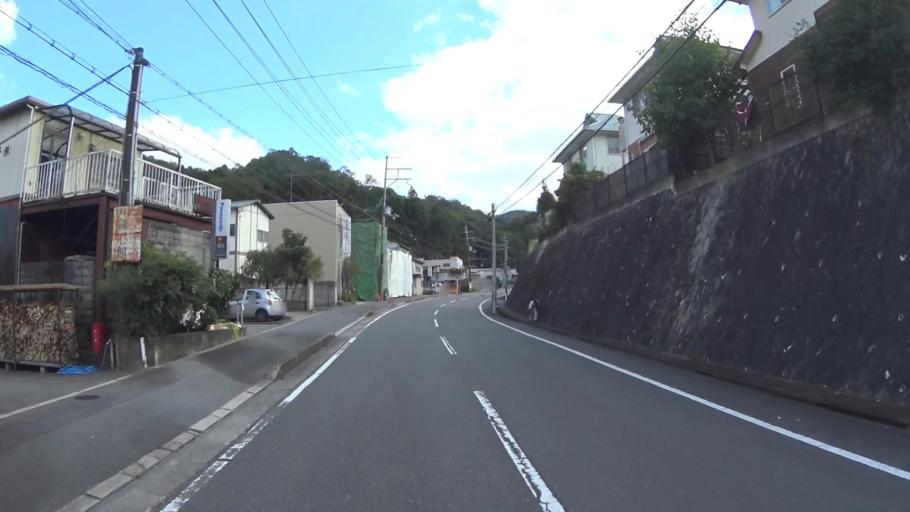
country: JP
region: Kyoto
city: Uji
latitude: 34.9274
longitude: 135.8170
